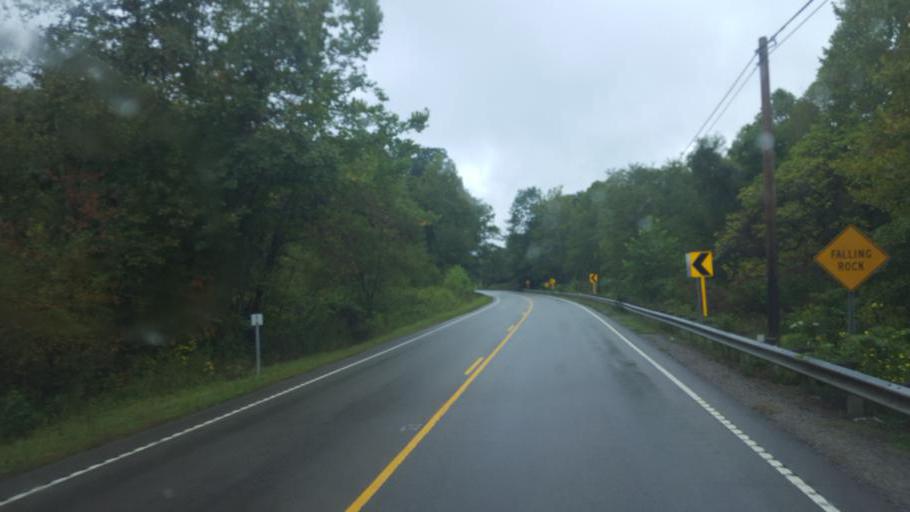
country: US
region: Ohio
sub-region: Jackson County
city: Oak Hill
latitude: 38.8412
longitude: -82.6391
